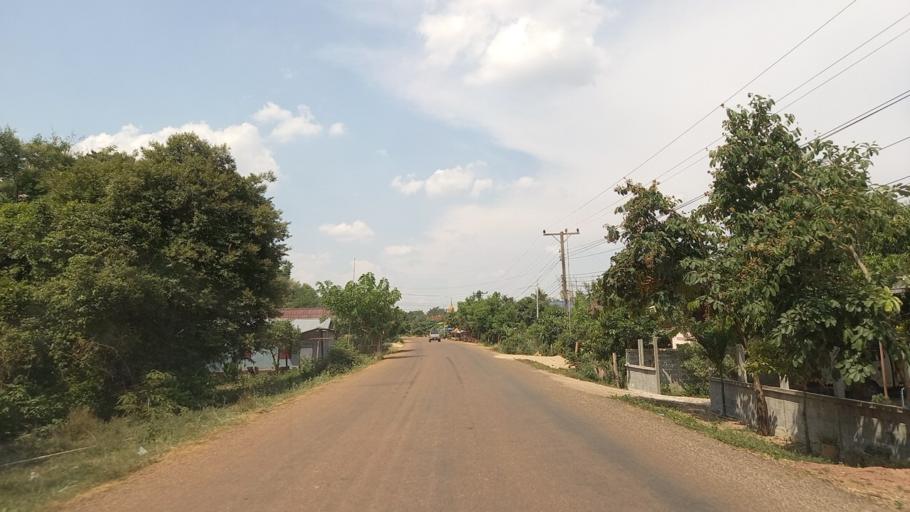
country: LA
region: Bolikhamxai
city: Muang Pakxan
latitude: 18.4064
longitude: 103.6995
